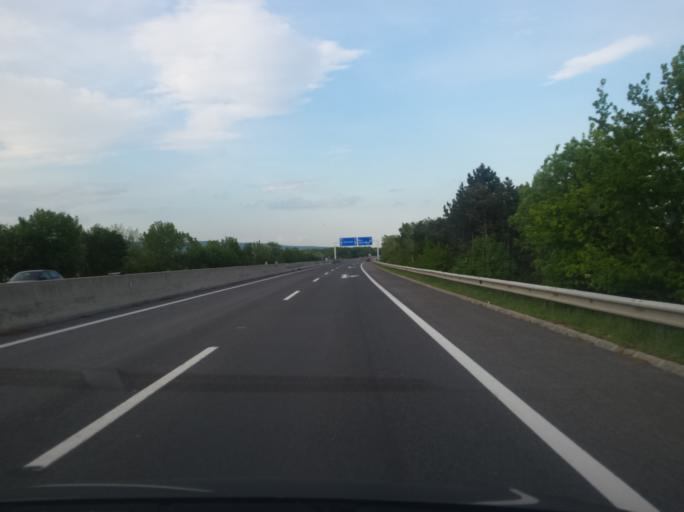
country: AT
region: Burgenland
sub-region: Eisenstadt-Umgebung
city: Wulkaprodersdorf
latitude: 47.8110
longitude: 16.4861
